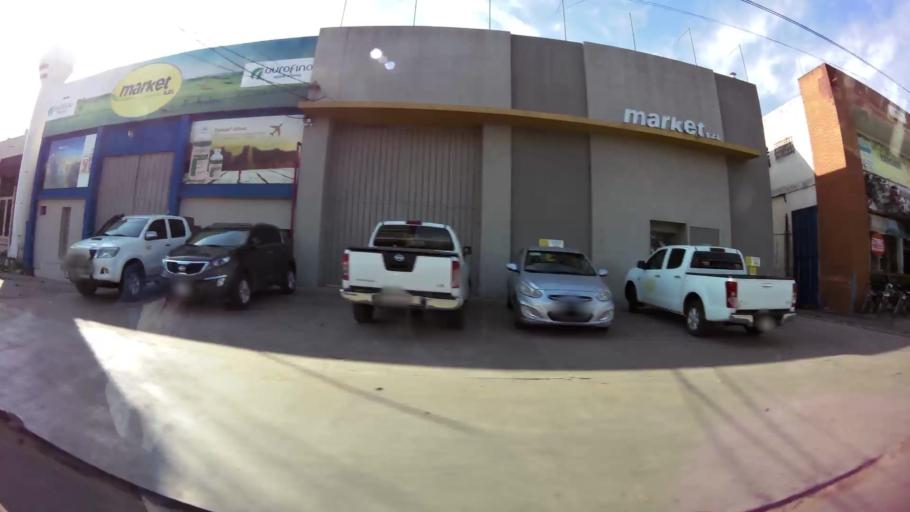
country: PY
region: Asuncion
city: Asuncion
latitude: -25.2719
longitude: -57.6049
